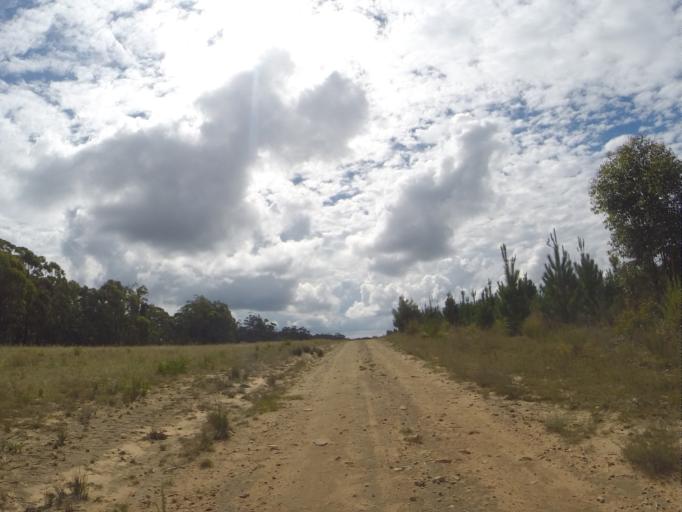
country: AU
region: New South Wales
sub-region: Wingecarribee
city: Moss Vale
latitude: -34.5138
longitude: 150.2272
